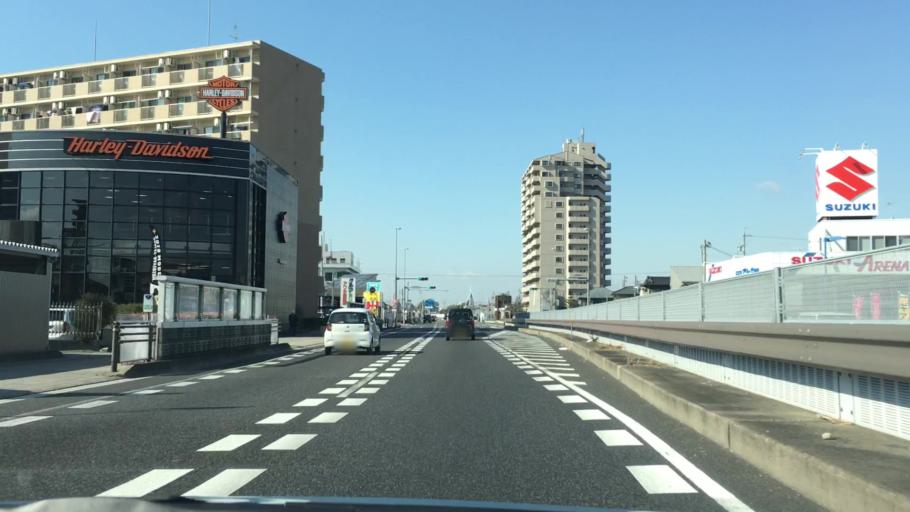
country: JP
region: Aichi
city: Okazaki
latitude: 34.9634
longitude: 137.1401
